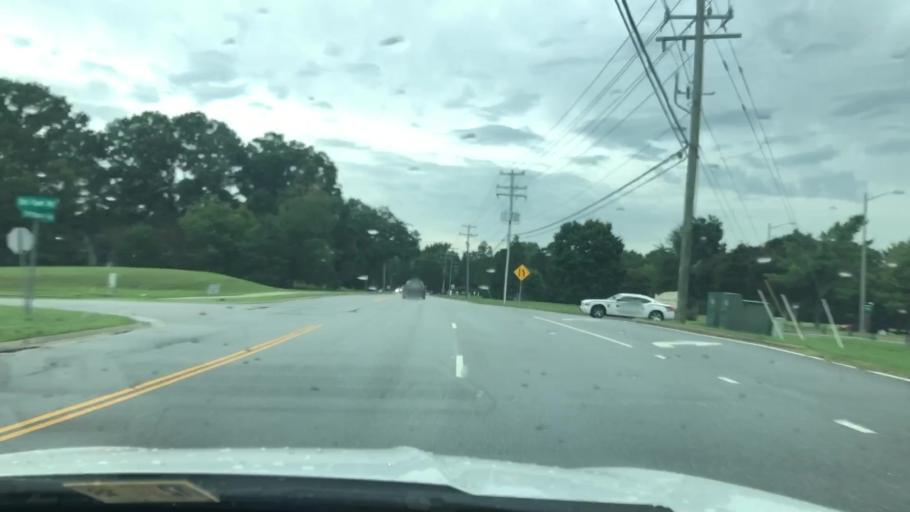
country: US
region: Virginia
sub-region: James City County
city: Williamsburg
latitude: 37.2680
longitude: -76.7585
